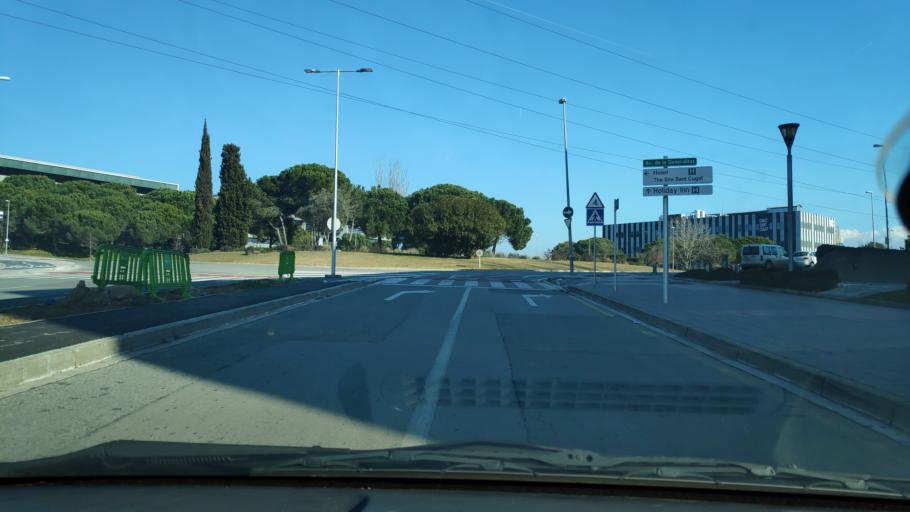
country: ES
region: Catalonia
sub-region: Provincia de Barcelona
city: Sant Cugat del Valles
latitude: 41.4919
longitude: 2.0738
